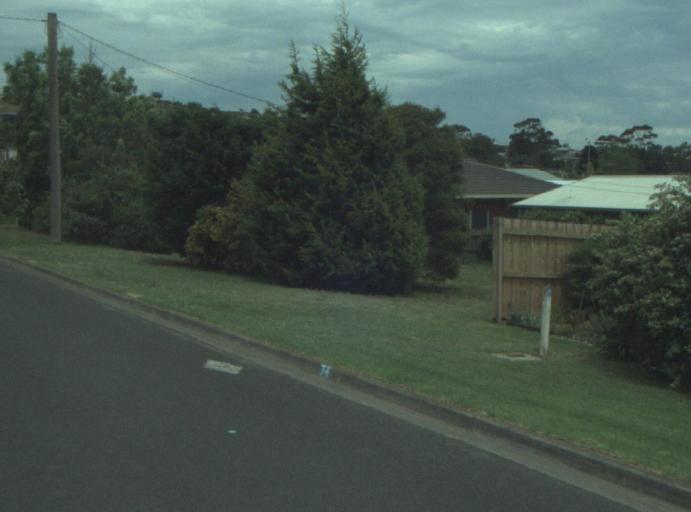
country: AU
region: Victoria
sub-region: Greater Geelong
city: Clifton Springs
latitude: -38.1190
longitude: 144.6453
